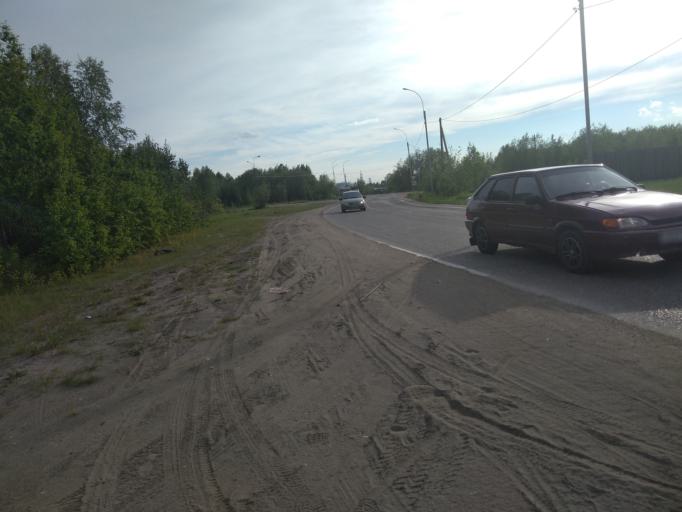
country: RU
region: Komi Republic
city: Pechora
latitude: 65.1459
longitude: 57.2076
